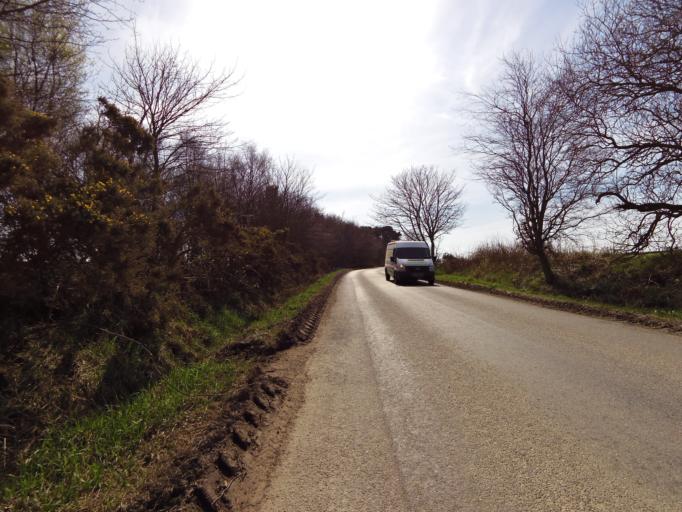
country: GB
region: Scotland
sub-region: Angus
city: Arbroath
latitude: 56.5805
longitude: -2.5577
